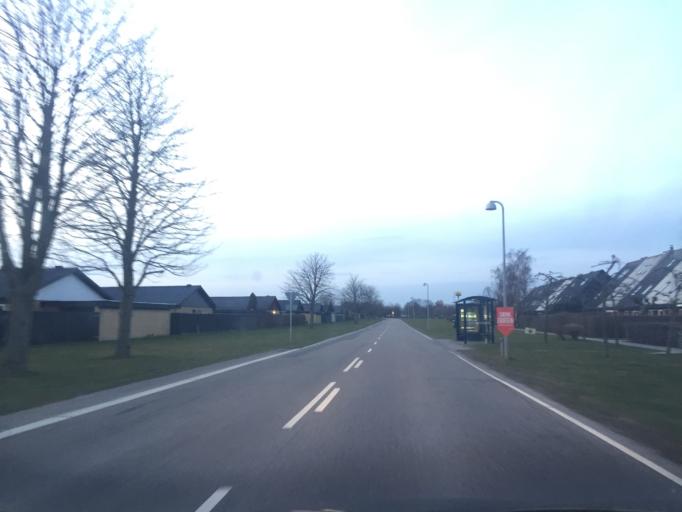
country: DK
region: Capital Region
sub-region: Hoje-Taastrup Kommune
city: Taastrup
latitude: 55.6382
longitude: 12.3086
